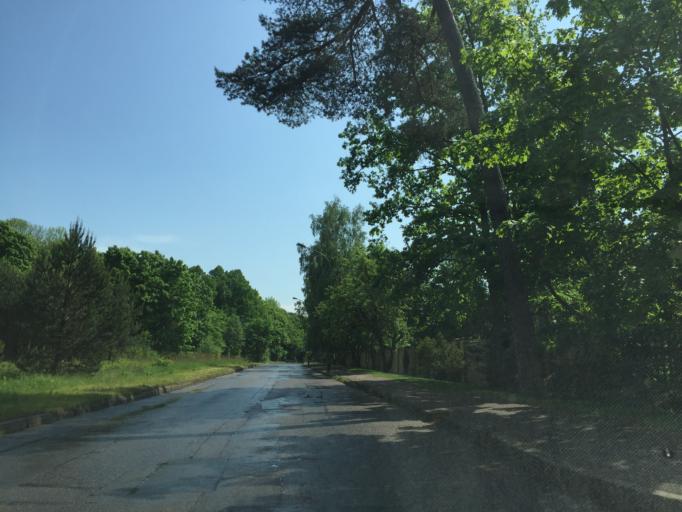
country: LT
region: Klaipedos apskritis
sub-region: Klaipeda
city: Klaipeda
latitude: 55.7696
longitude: 21.0844
